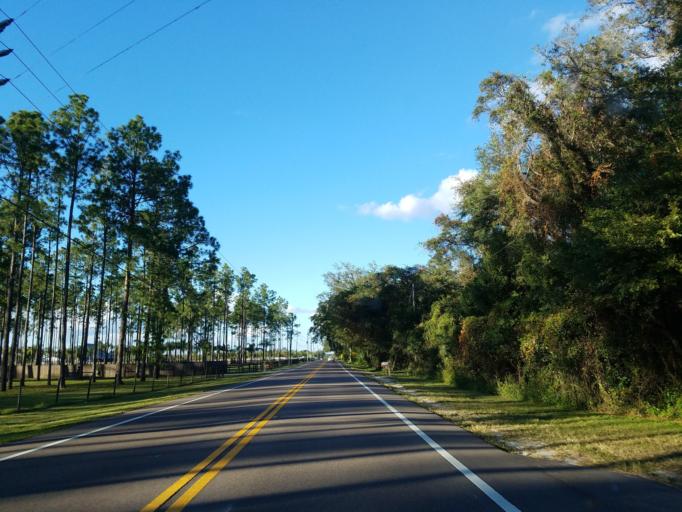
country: US
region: Florida
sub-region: Hernando County
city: Hill 'n Dale
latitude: 28.4361
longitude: -82.3028
